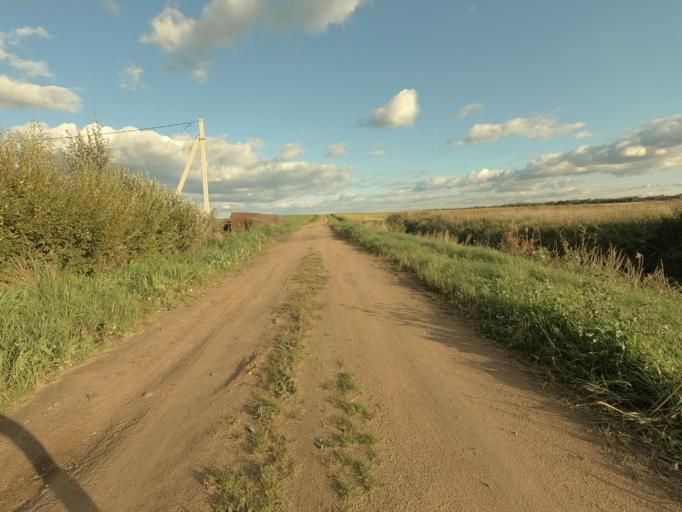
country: RU
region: Leningrad
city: Imeni Sverdlova
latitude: 59.8663
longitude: 30.7350
